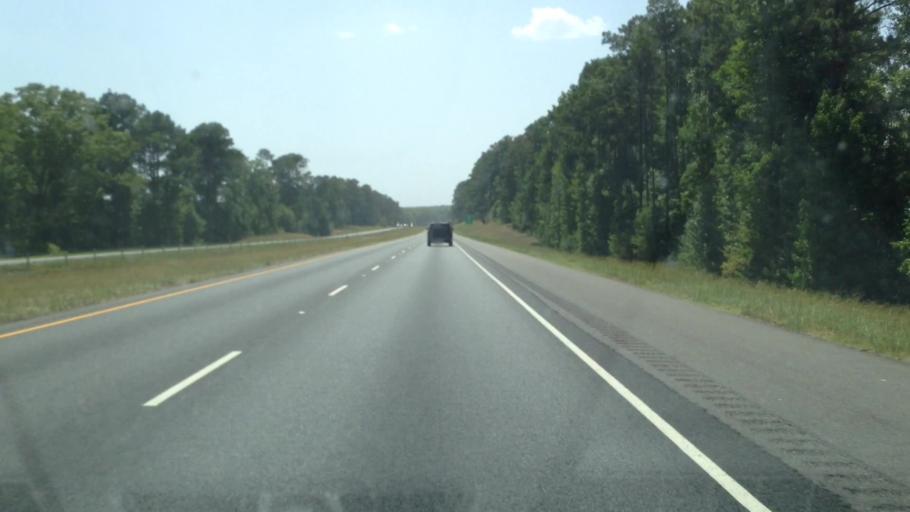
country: US
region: Louisiana
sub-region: Webster Parish
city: Minden
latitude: 32.5622
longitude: -93.1334
